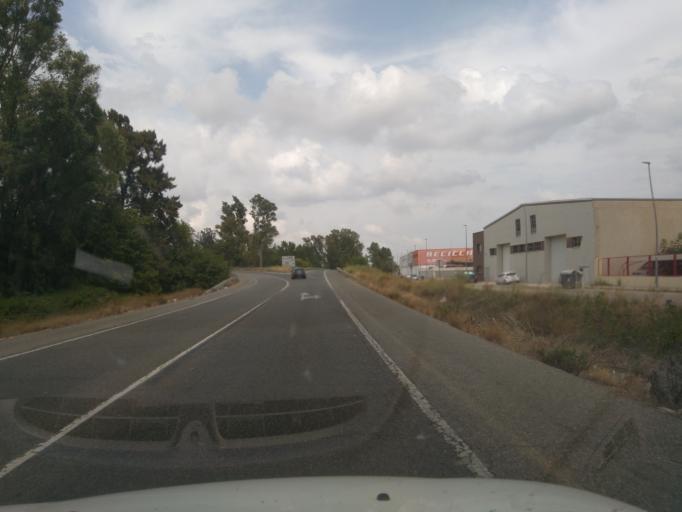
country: ES
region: Valencia
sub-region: Provincia de Valencia
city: Alzira
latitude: 39.1583
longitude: -0.4486
